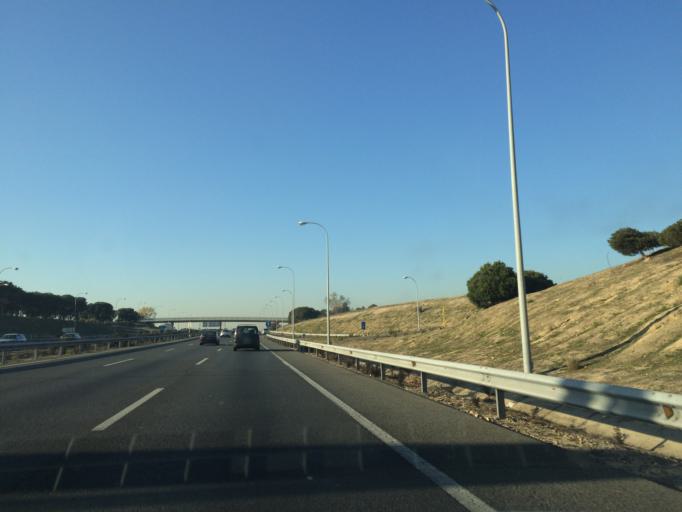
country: ES
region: Madrid
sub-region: Provincia de Madrid
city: Alcorcon
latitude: 40.3721
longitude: -3.8016
